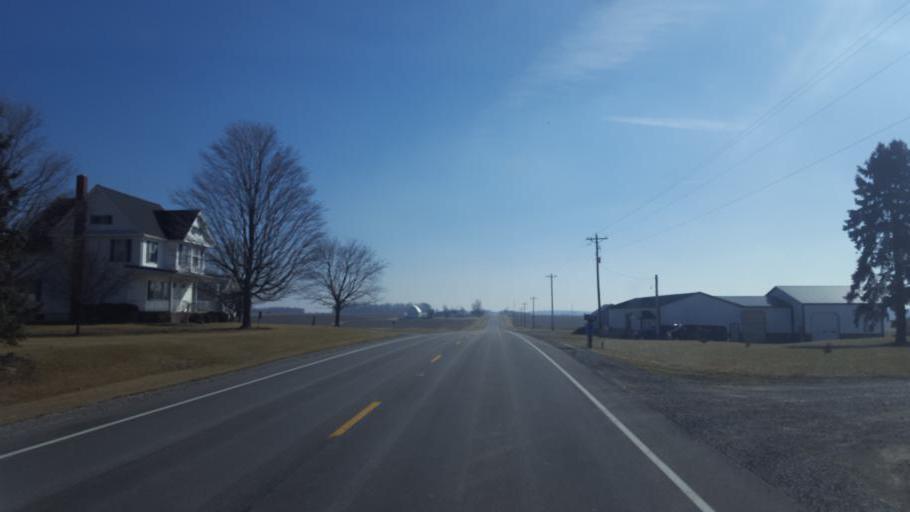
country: US
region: Ohio
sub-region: Huron County
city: Willard
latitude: 41.0542
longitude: -82.8574
